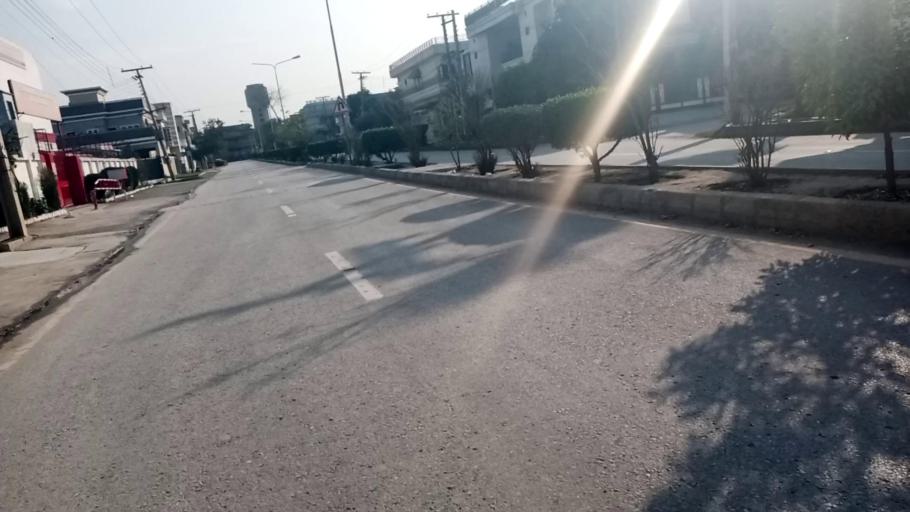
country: PK
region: Khyber Pakhtunkhwa
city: Peshawar
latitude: 33.9872
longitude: 71.4456
